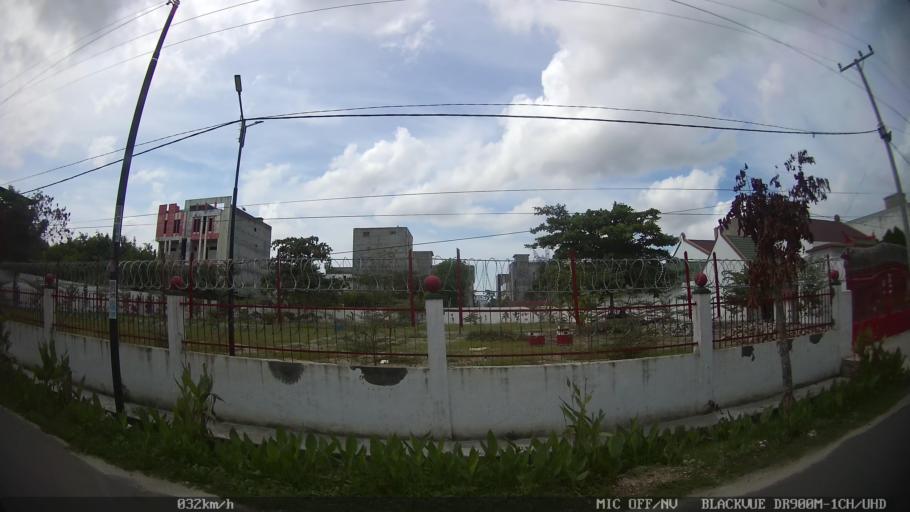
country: ID
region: North Sumatra
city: Percut
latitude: 3.5632
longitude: 98.8721
